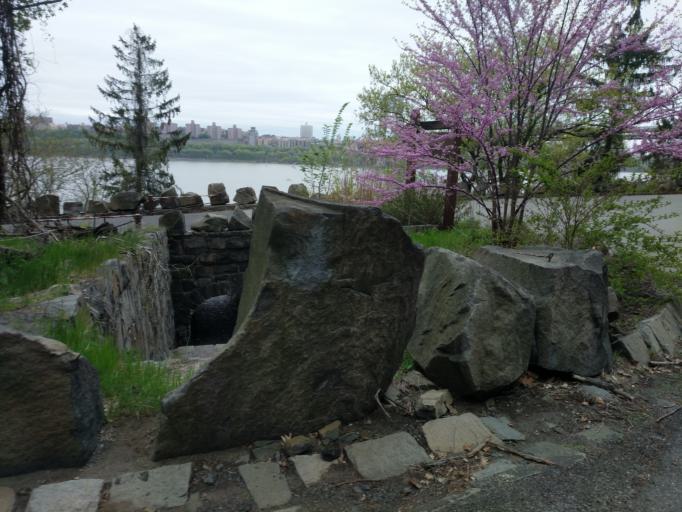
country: US
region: New Jersey
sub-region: Bergen County
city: Fort Lee
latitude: 40.8581
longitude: -73.9591
